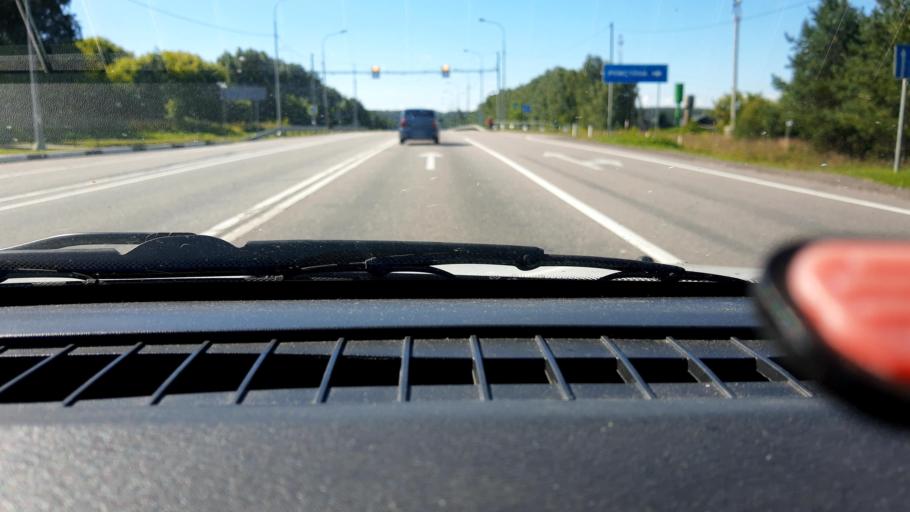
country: RU
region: Nizjnij Novgorod
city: Surovatikha
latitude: 55.7145
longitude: 43.9891
